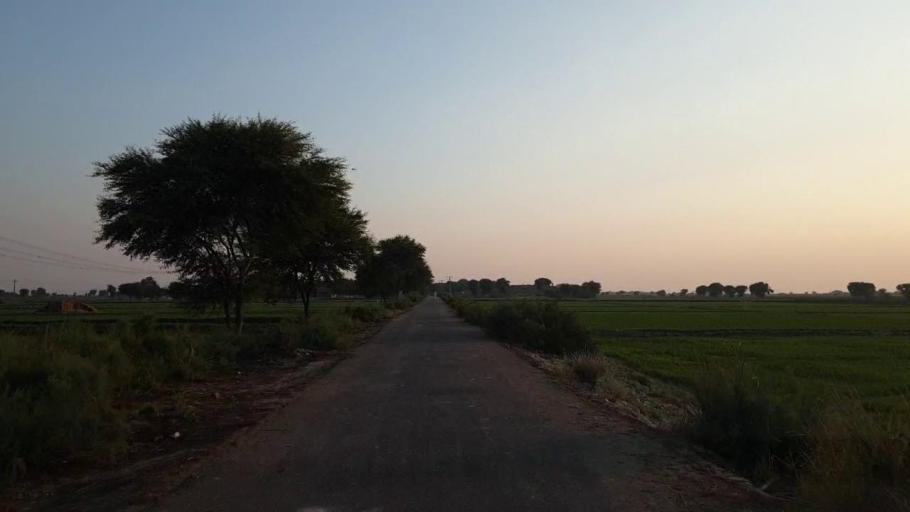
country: PK
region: Sindh
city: Sehwan
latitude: 26.4464
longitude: 67.7618
